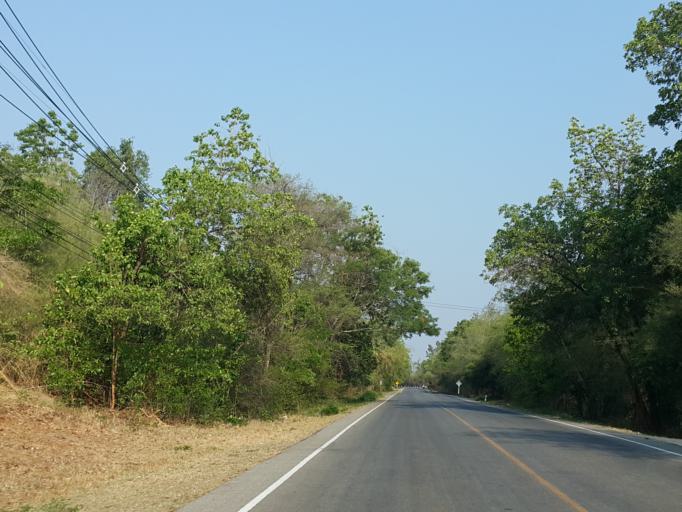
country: TH
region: Kanchanaburi
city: Sai Yok
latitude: 14.2207
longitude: 99.1734
